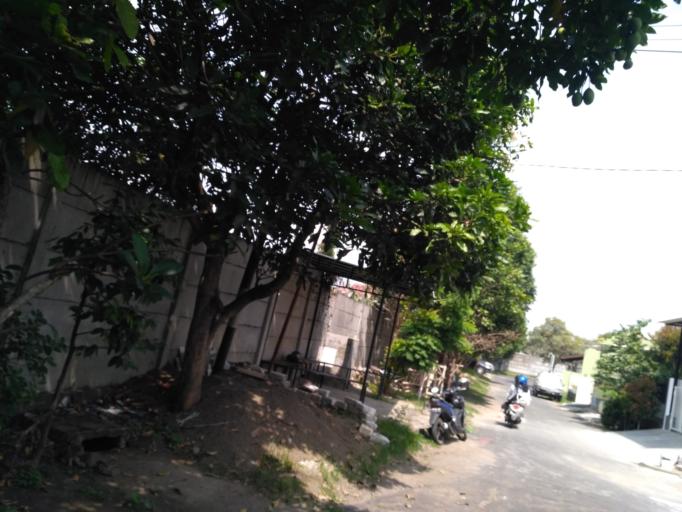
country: ID
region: East Java
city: Malang
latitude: -7.9311
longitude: 112.6134
